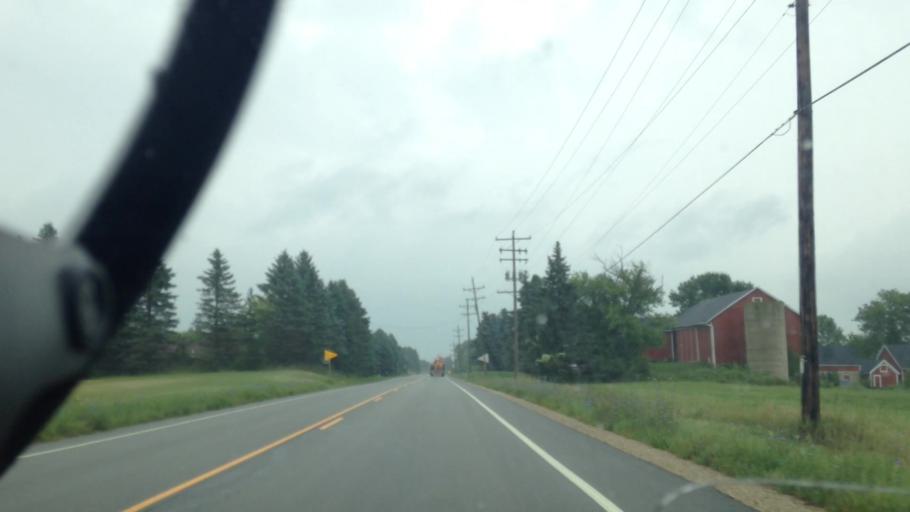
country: US
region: Wisconsin
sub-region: Washington County
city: Slinger
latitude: 43.3202
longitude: -88.2676
